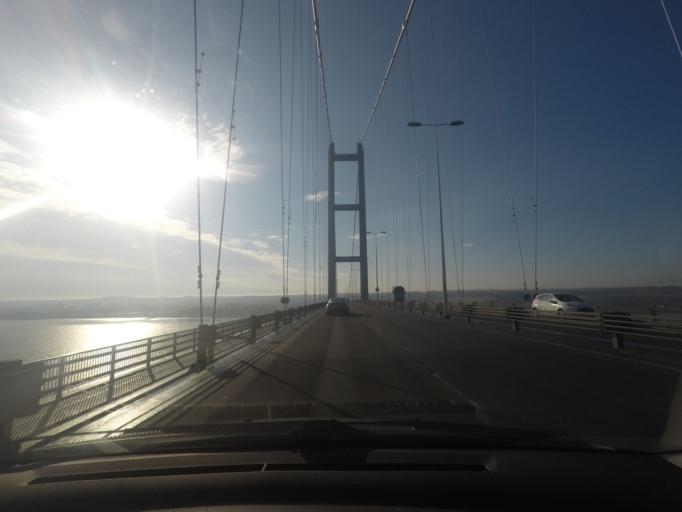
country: GB
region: England
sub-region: East Riding of Yorkshire
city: Hessle
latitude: 53.7043
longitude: -0.4495
